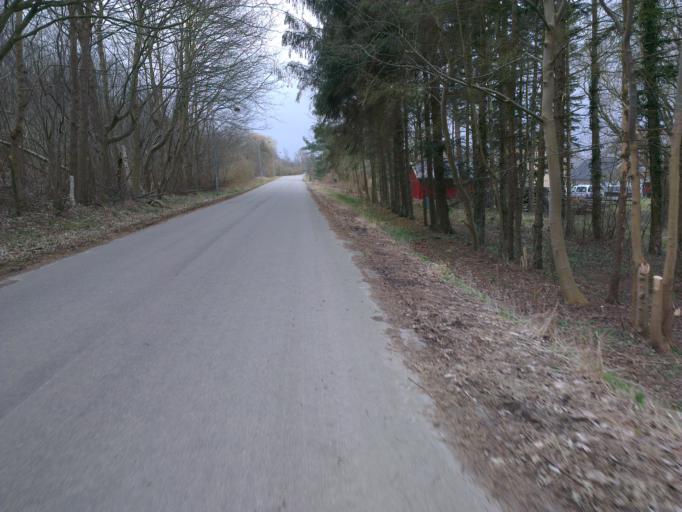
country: DK
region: Capital Region
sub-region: Frederikssund Kommune
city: Frederikssund
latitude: 55.8809
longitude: 12.0702
